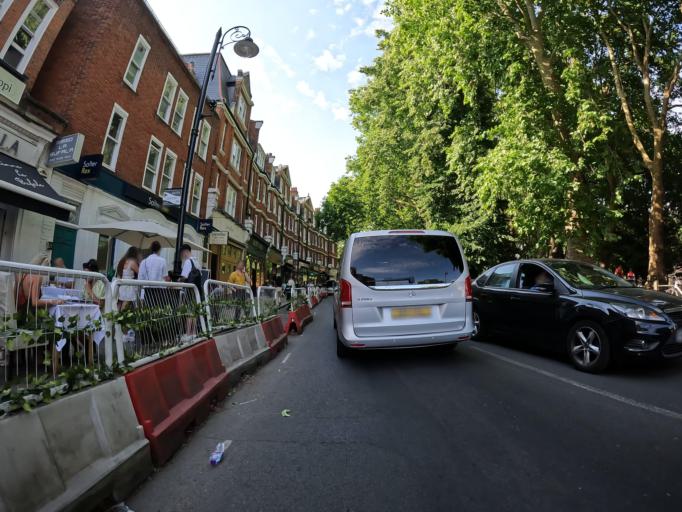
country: GB
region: England
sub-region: Greater London
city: Barnet
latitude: 51.6431
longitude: -0.1933
